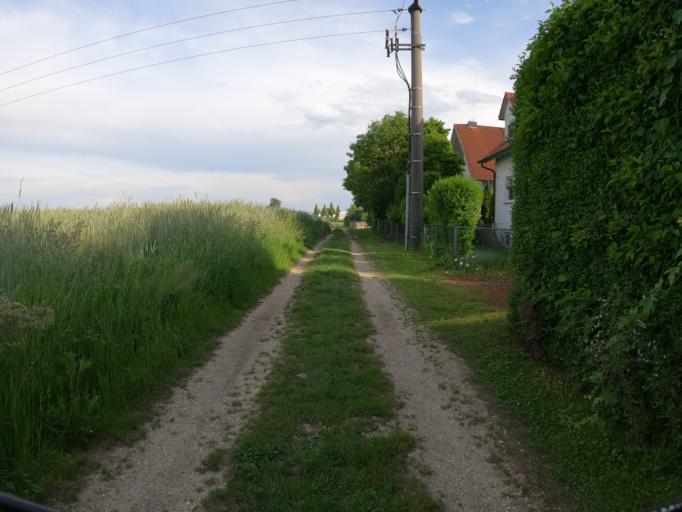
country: DE
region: Bavaria
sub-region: Swabia
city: Neu-Ulm
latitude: 48.4165
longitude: 10.0417
